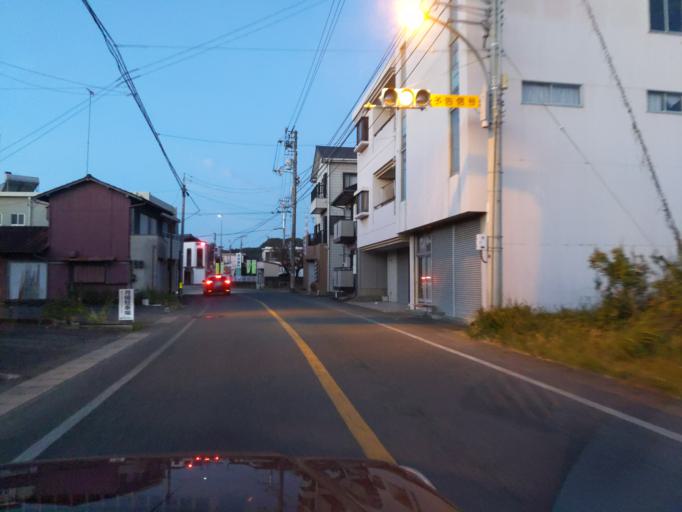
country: JP
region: Tokushima
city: Anan
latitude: 33.8896
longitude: 134.6536
